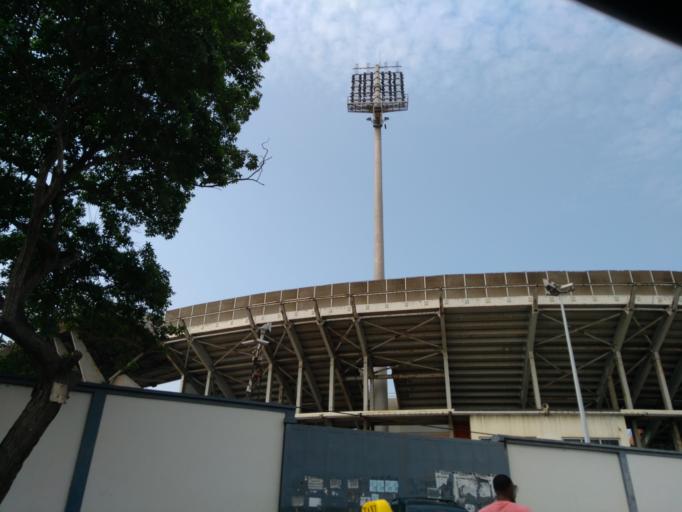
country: GH
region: Greater Accra
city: Accra
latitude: 5.5504
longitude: -0.1927
